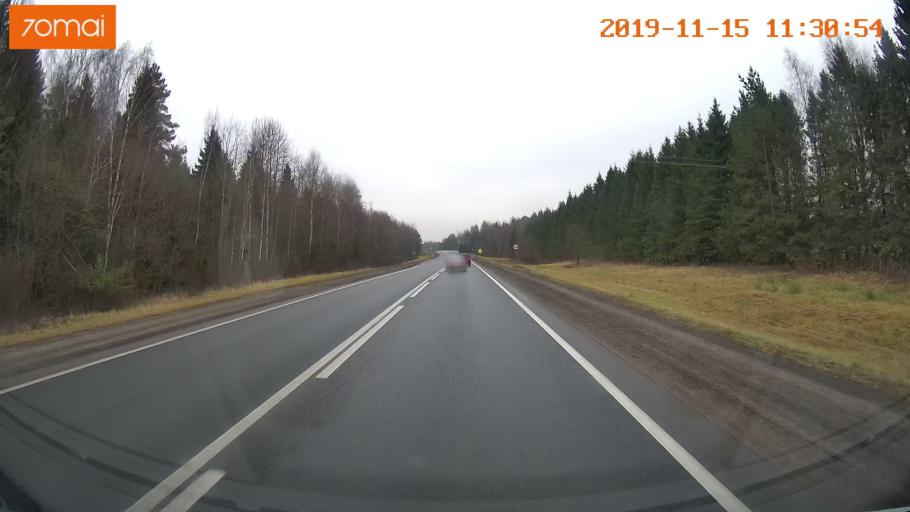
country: RU
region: Vologda
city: Molochnoye
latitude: 59.1786
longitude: 39.5356
